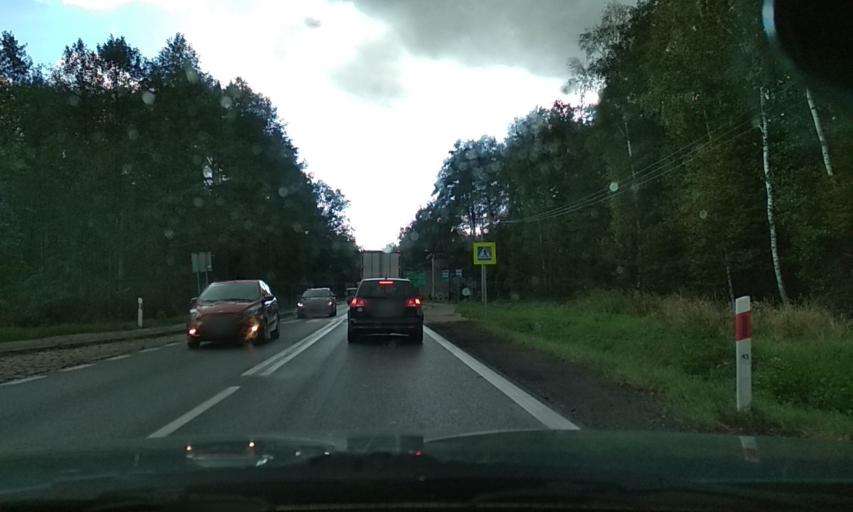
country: PL
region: Silesian Voivodeship
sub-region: Powiat gliwicki
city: Wilcza
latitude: 50.2166
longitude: 18.6020
